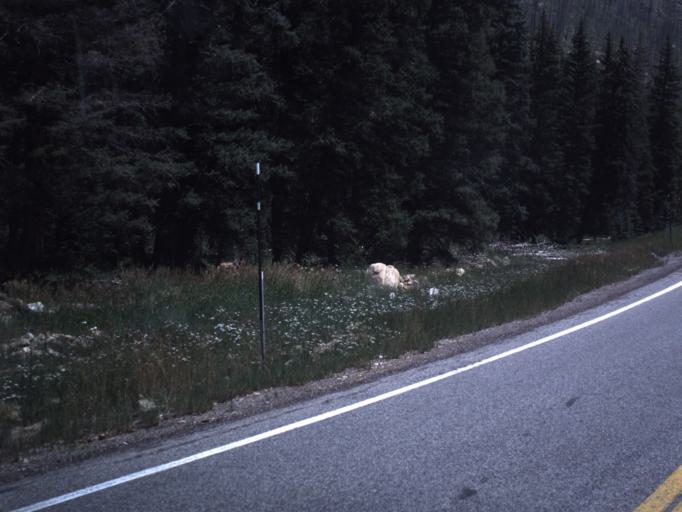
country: US
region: Utah
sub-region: Sanpete County
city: Fairview
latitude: 39.5470
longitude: -111.1668
